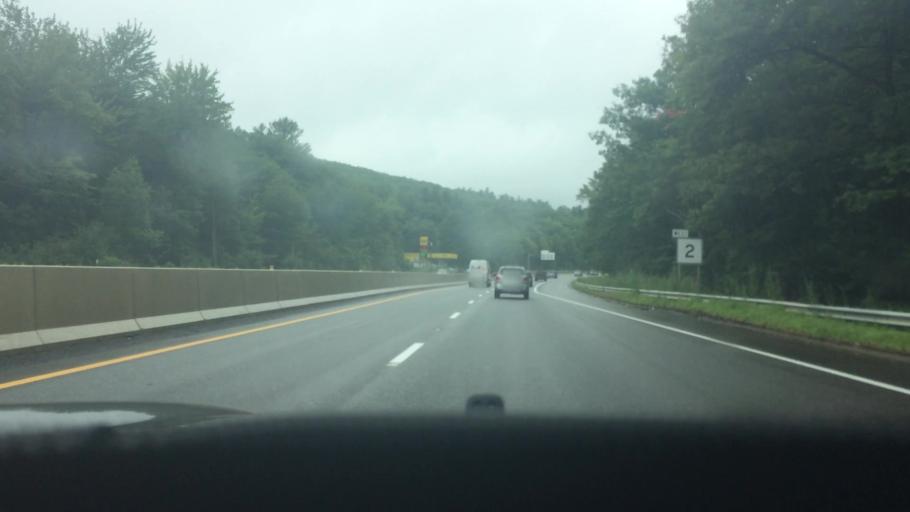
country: US
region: Massachusetts
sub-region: Worcester County
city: Fitchburg
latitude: 42.5514
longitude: -71.7868
